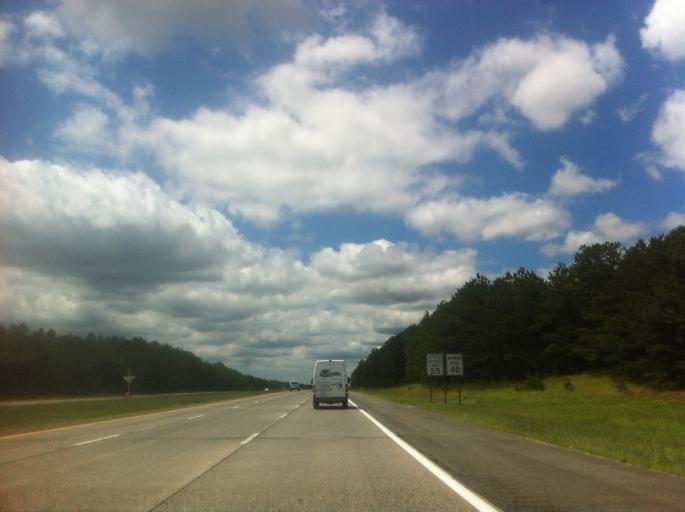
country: US
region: New York
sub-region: Suffolk County
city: Calverton
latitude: 40.8900
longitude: -72.7547
